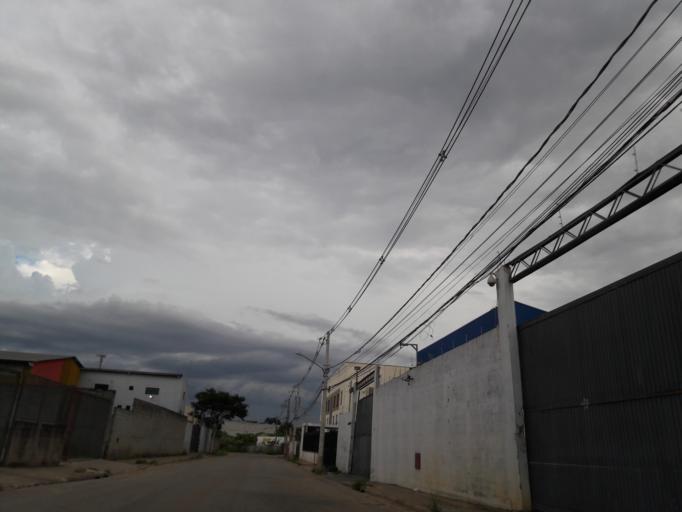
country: BR
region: Sao Paulo
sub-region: Aruja
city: Aruja
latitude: -23.4143
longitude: -46.3972
